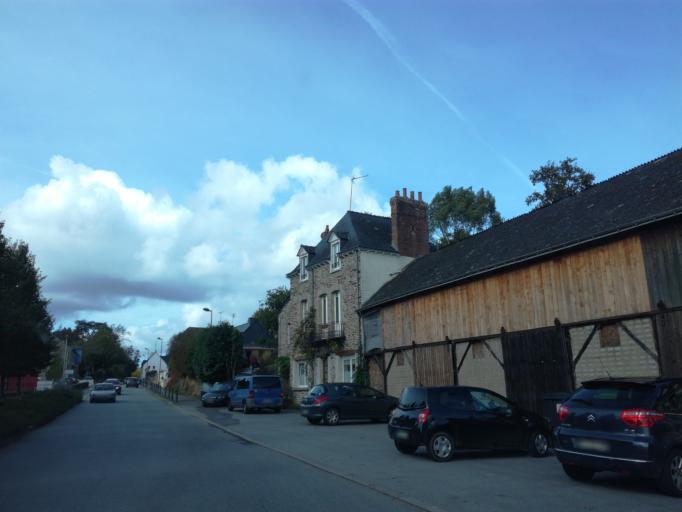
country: FR
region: Brittany
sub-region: Departement du Morbihan
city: Rohan
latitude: 48.0707
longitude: -2.7506
